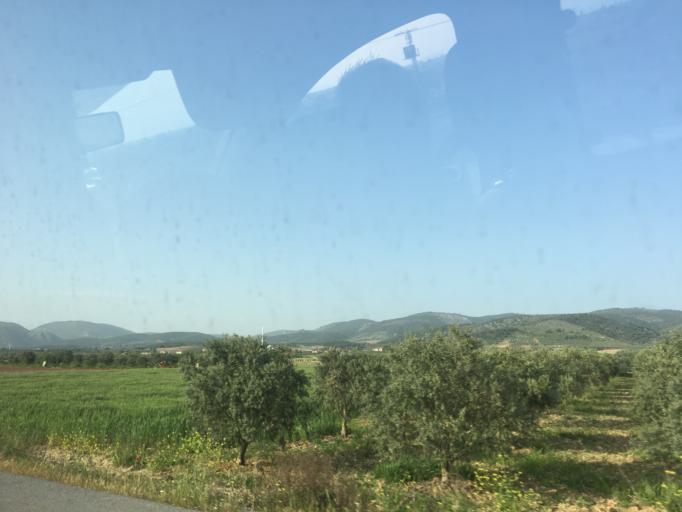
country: TR
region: Manisa
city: Golmarmara
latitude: 38.7880
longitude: 27.9031
